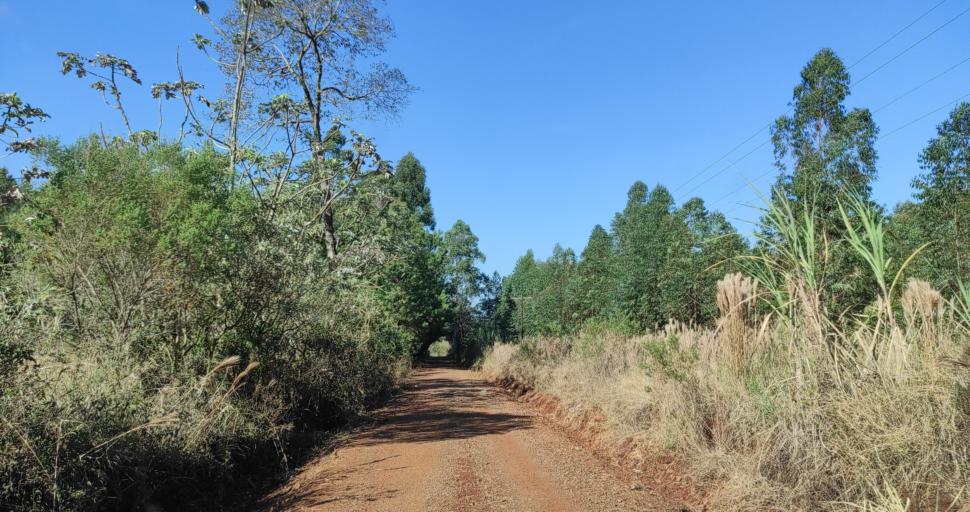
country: AR
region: Misiones
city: Capiovi
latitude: -26.8923
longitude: -55.0382
